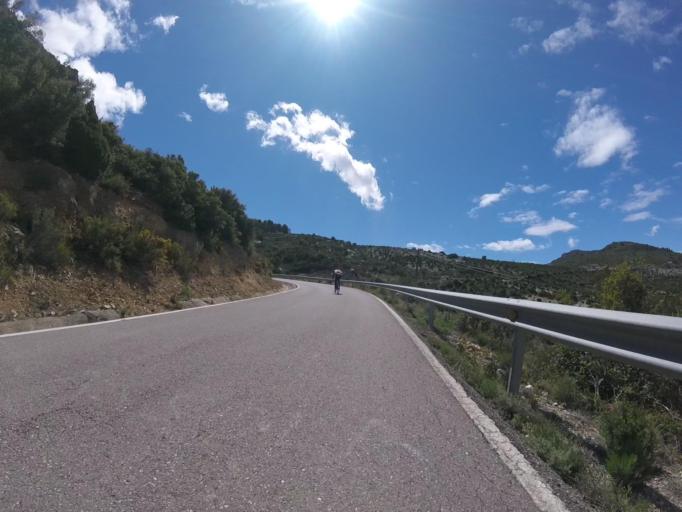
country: ES
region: Valencia
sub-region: Provincia de Castello
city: Sierra-Engarceran
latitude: 40.2831
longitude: -0.0327
